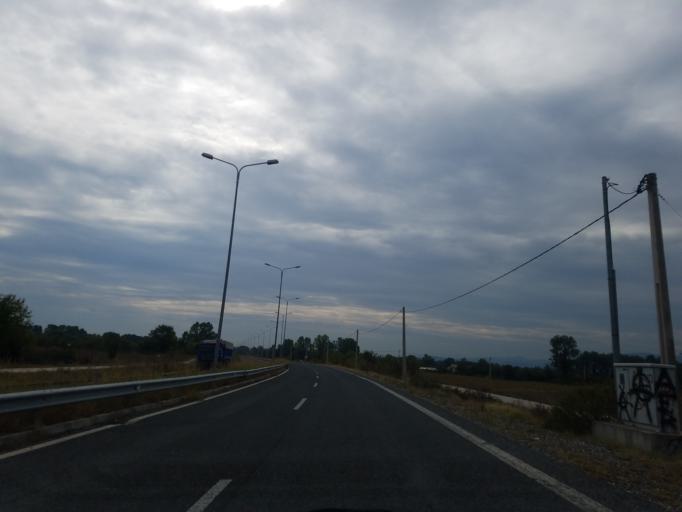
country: GR
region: Thessaly
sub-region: Trikala
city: Pyrgetos
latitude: 39.5371
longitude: 21.7368
